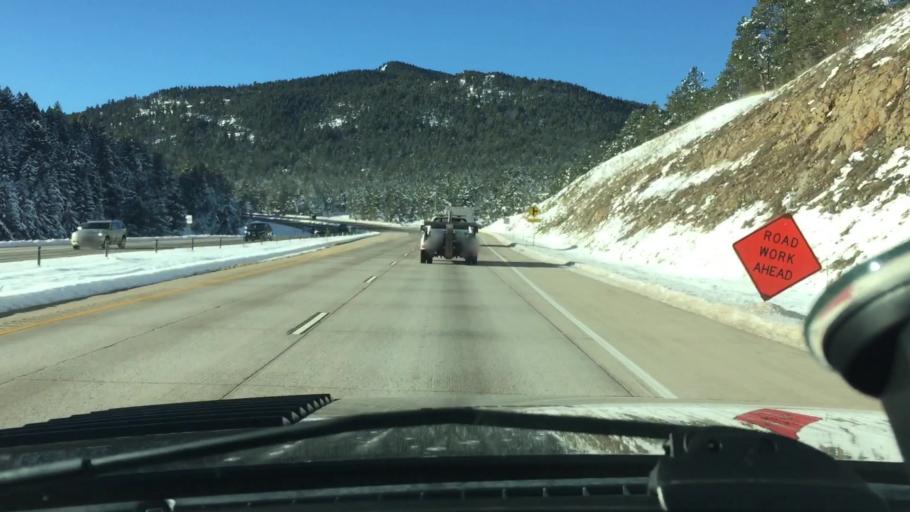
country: US
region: Colorado
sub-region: Jefferson County
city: Indian Hills
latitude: 39.5775
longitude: -105.2369
